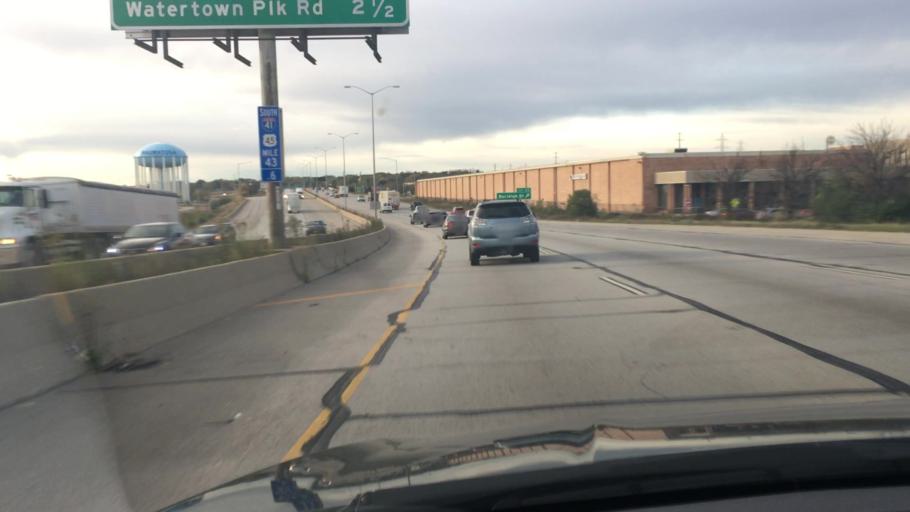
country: US
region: Wisconsin
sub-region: Waukesha County
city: Butler
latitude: 43.0804
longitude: -88.0580
